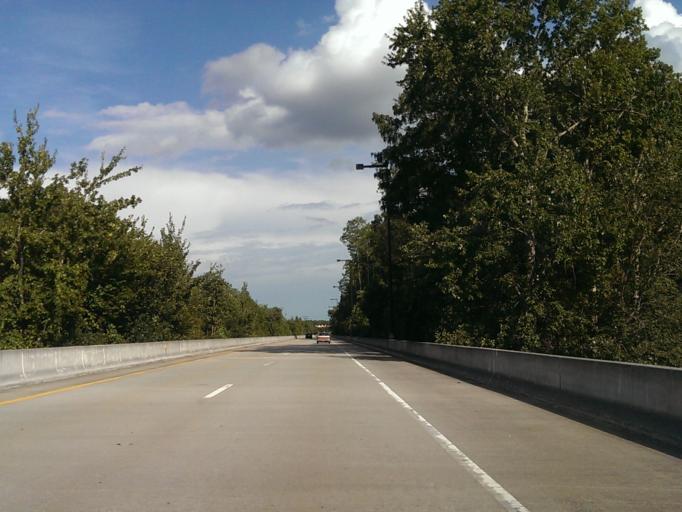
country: US
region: Florida
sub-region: Osceola County
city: Celebration
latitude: 28.3645
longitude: -81.5834
